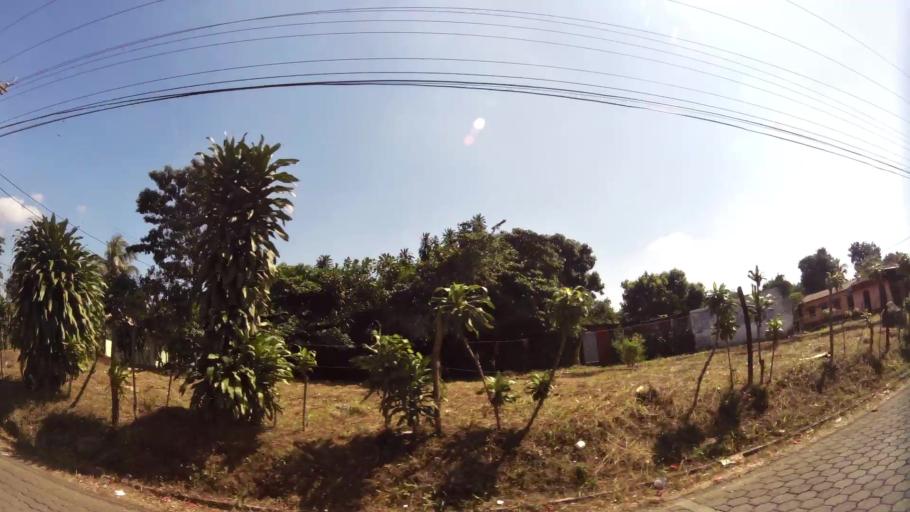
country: GT
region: Suchitepeque
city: Mazatenango
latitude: 14.5288
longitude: -91.4825
